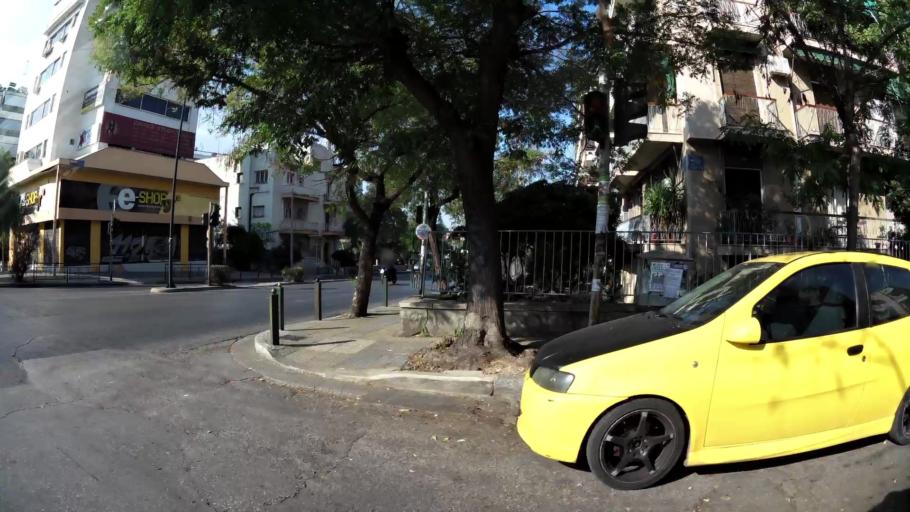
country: GR
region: Attica
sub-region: Nomarchia Athinas
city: Galatsi
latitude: 38.0159
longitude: 23.7409
